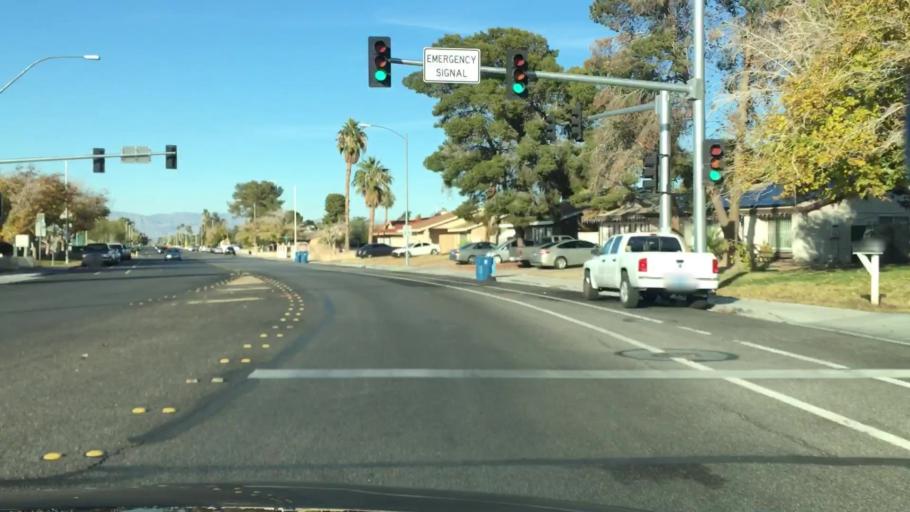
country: US
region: Nevada
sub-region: Clark County
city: Paradise
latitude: 36.0886
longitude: -115.1279
